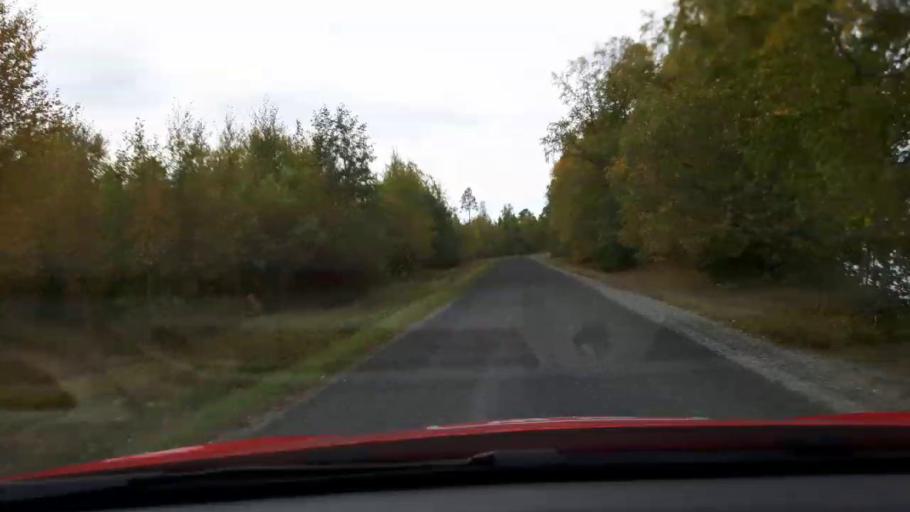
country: SE
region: Jaemtland
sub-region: Krokoms Kommun
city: Krokom
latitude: 63.1616
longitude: 14.1490
